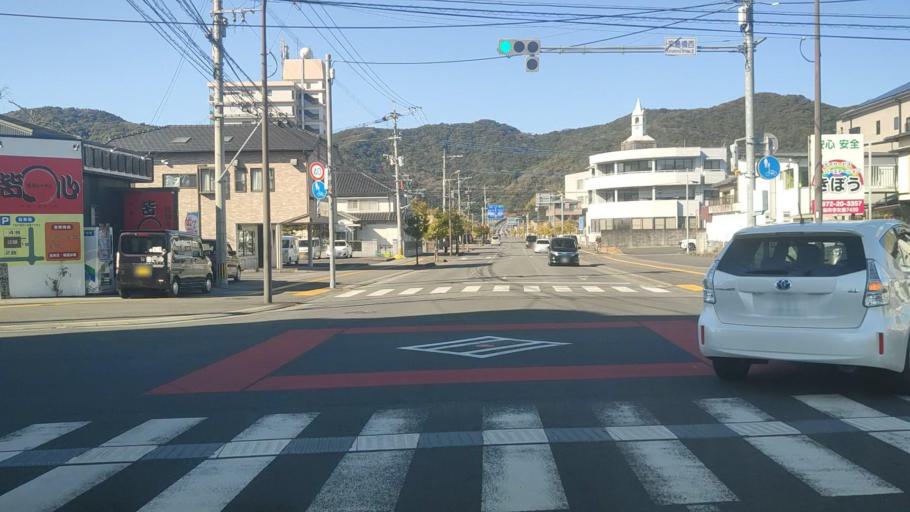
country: JP
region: Oita
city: Saiki
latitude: 32.9603
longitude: 131.9015
